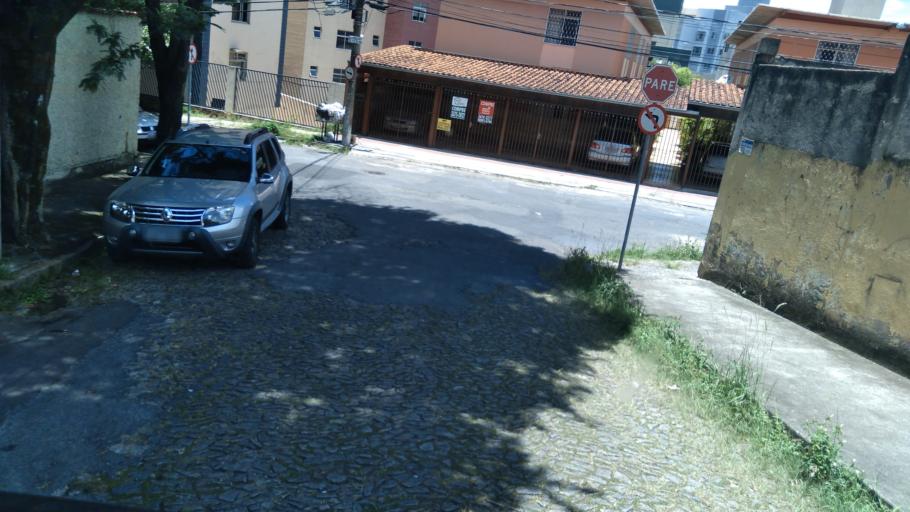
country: BR
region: Minas Gerais
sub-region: Belo Horizonte
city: Belo Horizonte
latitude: -19.9179
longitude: -43.9885
